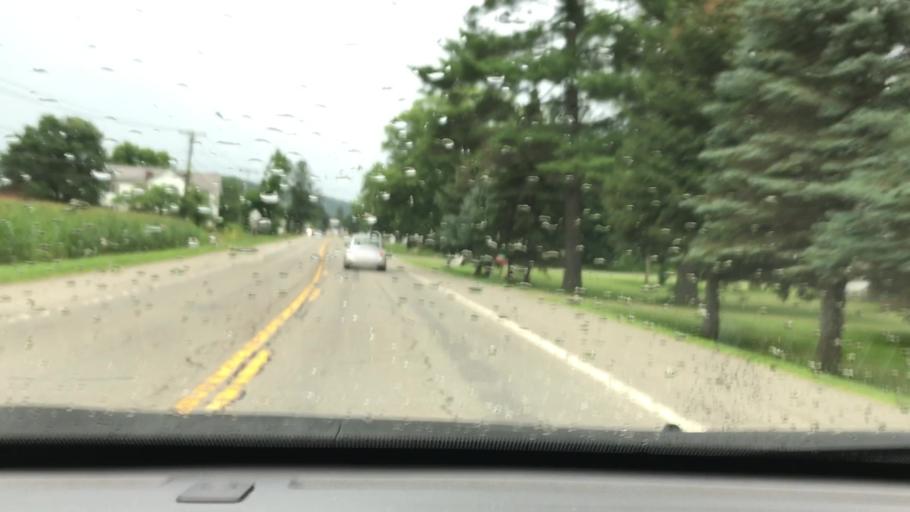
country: US
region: New York
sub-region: Cattaraugus County
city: Salamanca
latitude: 42.1938
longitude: -78.6608
